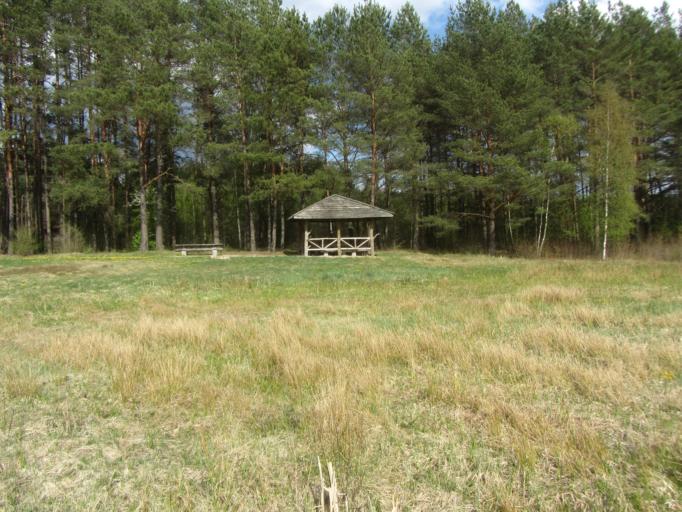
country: LT
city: Salcininkai
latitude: 54.2213
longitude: 25.5997
